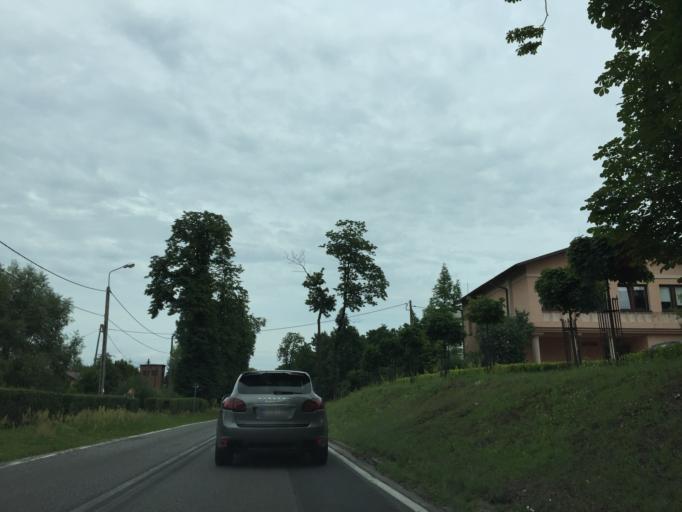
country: PL
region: Lesser Poland Voivodeship
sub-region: Powiat olkuski
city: Klucze
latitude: 50.3387
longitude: 19.5621
